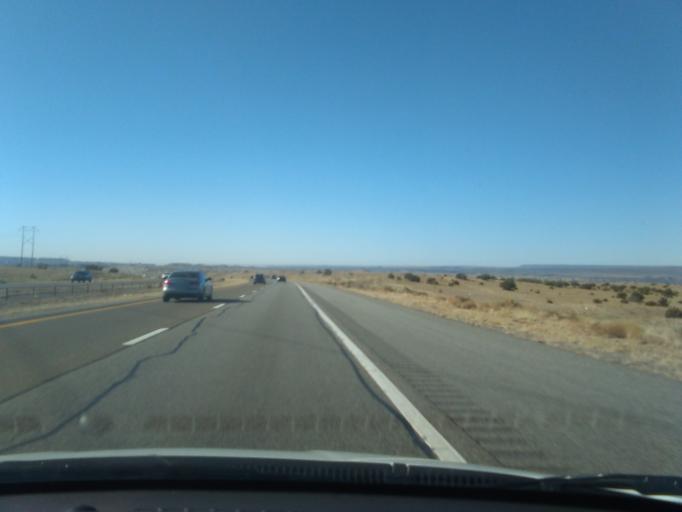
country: US
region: New Mexico
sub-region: Sandoval County
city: Santo Domingo Pueblo
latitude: 35.4477
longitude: -106.3596
